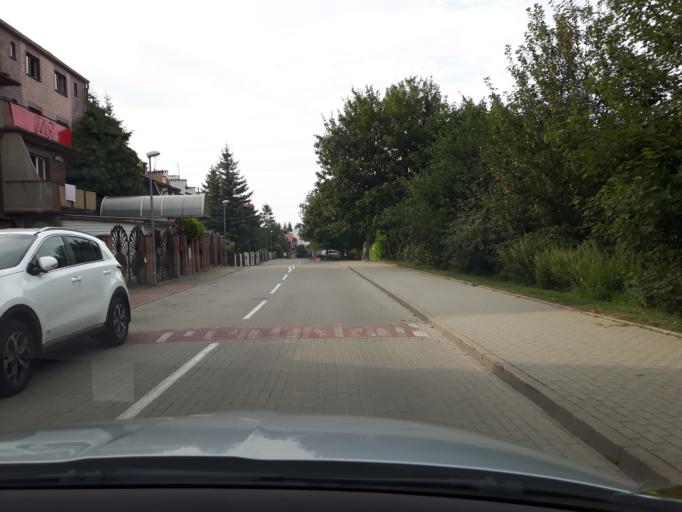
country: PL
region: Pomeranian Voivodeship
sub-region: Gdynia
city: Gdynia
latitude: 54.5015
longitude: 18.5486
